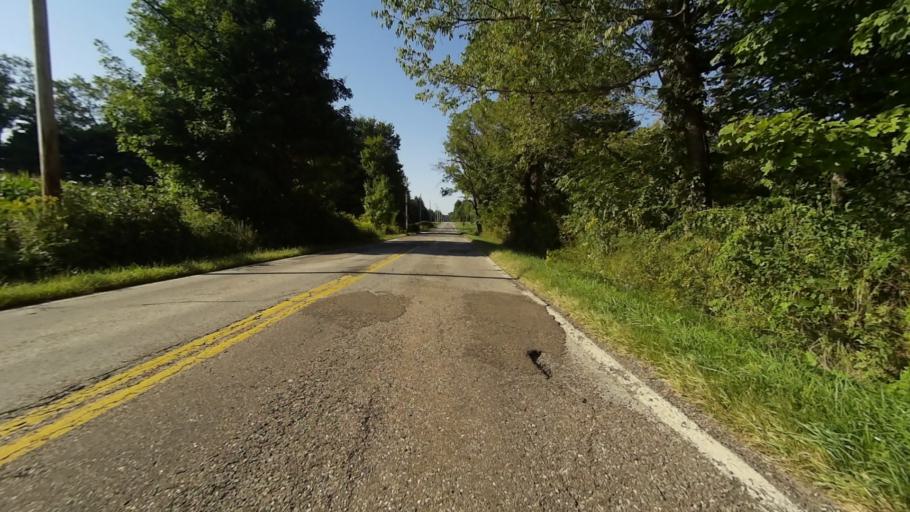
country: US
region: Ohio
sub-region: Portage County
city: Streetsboro
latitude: 41.2246
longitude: -81.3121
